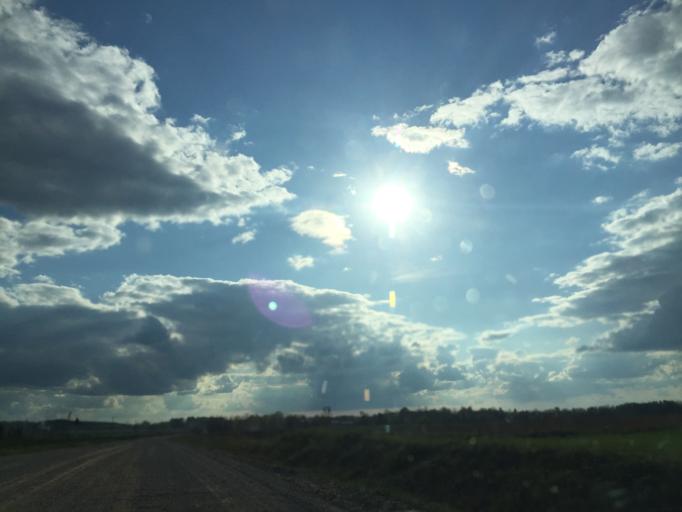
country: LV
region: Beverina
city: Murmuiza
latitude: 57.3987
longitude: 25.4719
